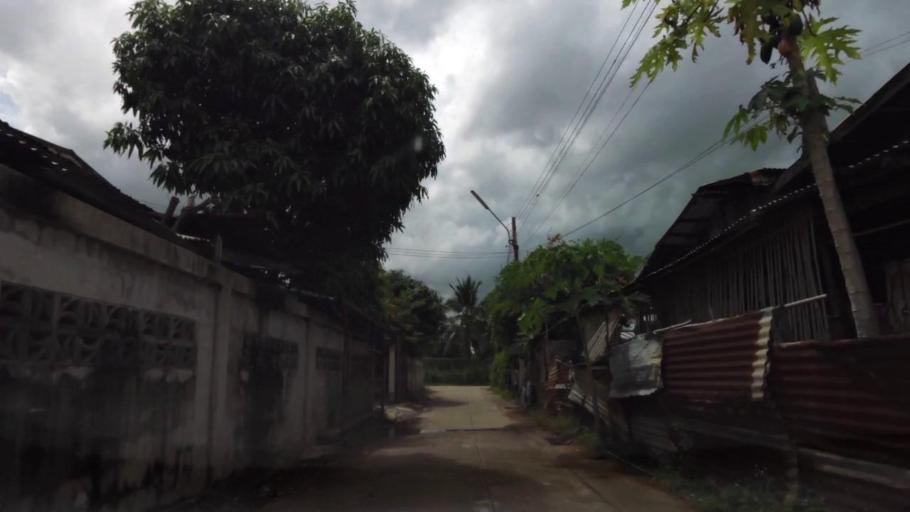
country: TH
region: Nakhon Sawan
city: Phai Sali
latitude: 15.6003
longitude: 100.6519
